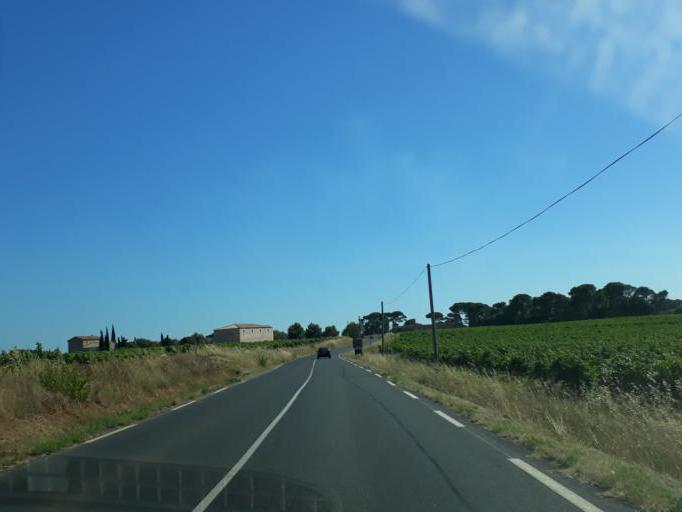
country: FR
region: Languedoc-Roussillon
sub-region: Departement de l'Herault
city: Agde
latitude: 43.3459
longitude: 3.4880
